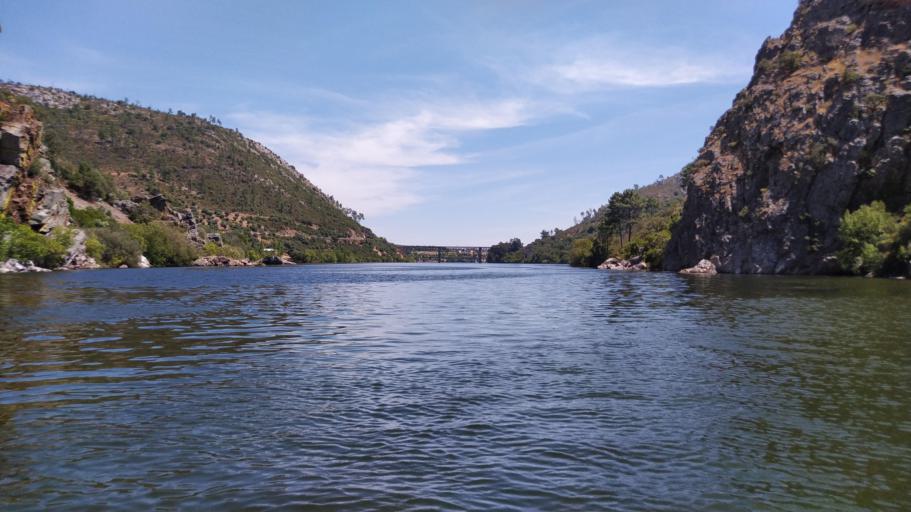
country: PT
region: Portalegre
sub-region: Nisa
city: Nisa
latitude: 39.6431
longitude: -7.6875
